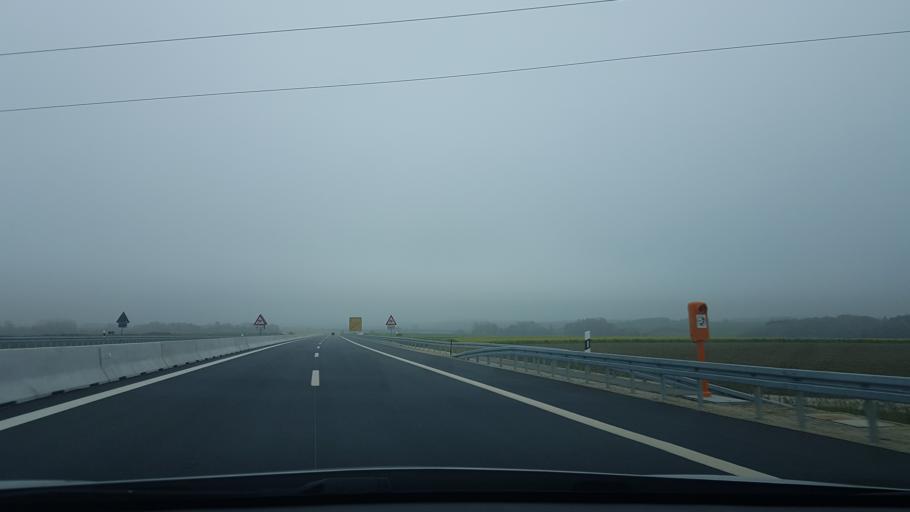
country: DE
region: Bavaria
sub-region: Lower Bavaria
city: Buch
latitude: 48.6605
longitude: 12.1874
